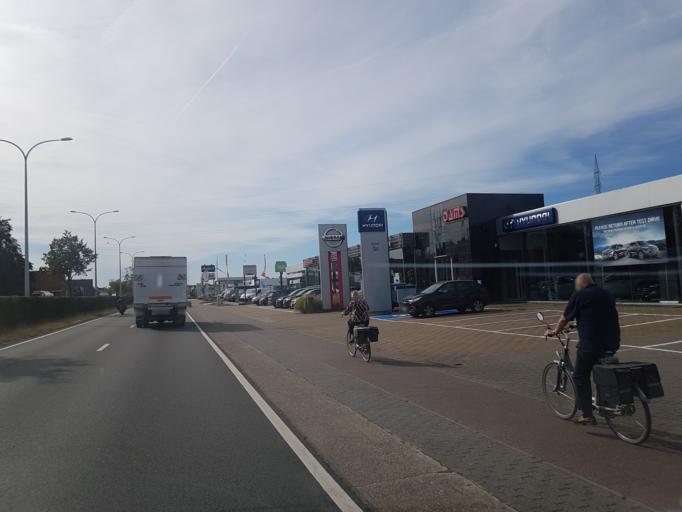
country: BE
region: Flanders
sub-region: Provincie Antwerpen
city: Geel
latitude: 51.1468
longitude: 4.9590
